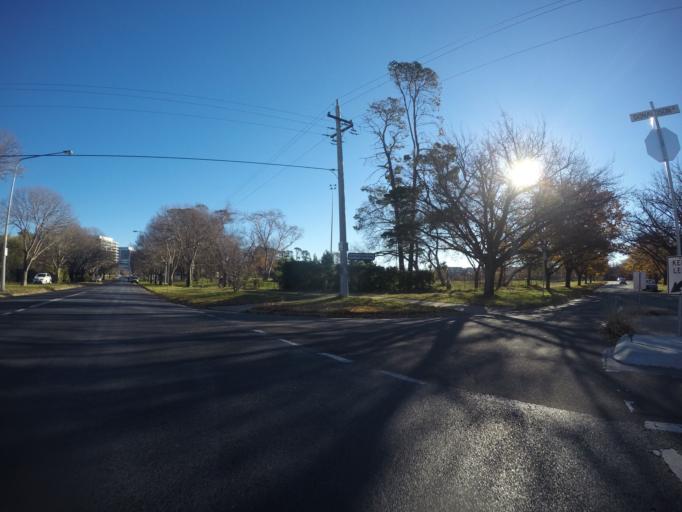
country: AU
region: Australian Capital Territory
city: Canberra
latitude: -35.2751
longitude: 149.1369
